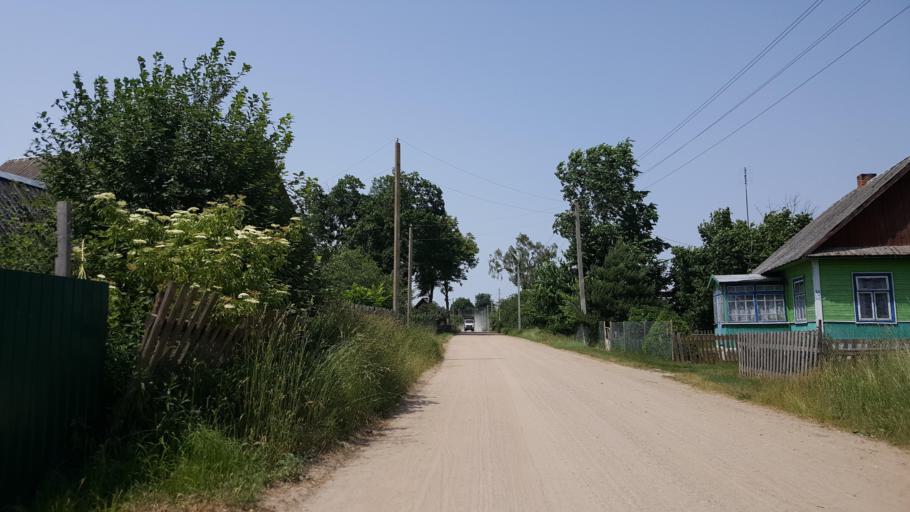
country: BY
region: Brest
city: Kamyanyets
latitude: 52.4770
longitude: 23.8855
